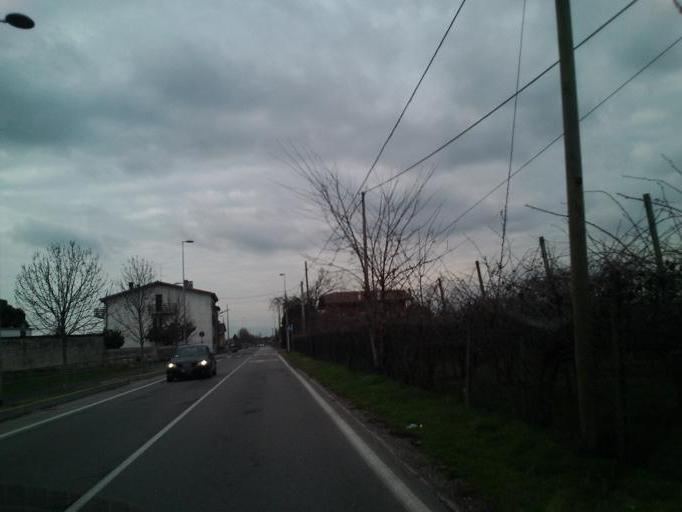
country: IT
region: Veneto
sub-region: Provincia di Verona
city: Alpo
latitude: 45.3803
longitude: 10.9195
